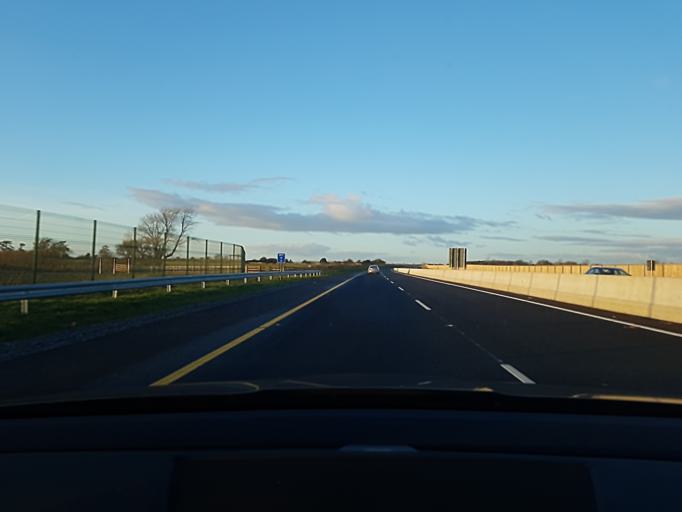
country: IE
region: Connaught
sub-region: County Galway
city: Athenry
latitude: 53.3229
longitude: -8.8028
